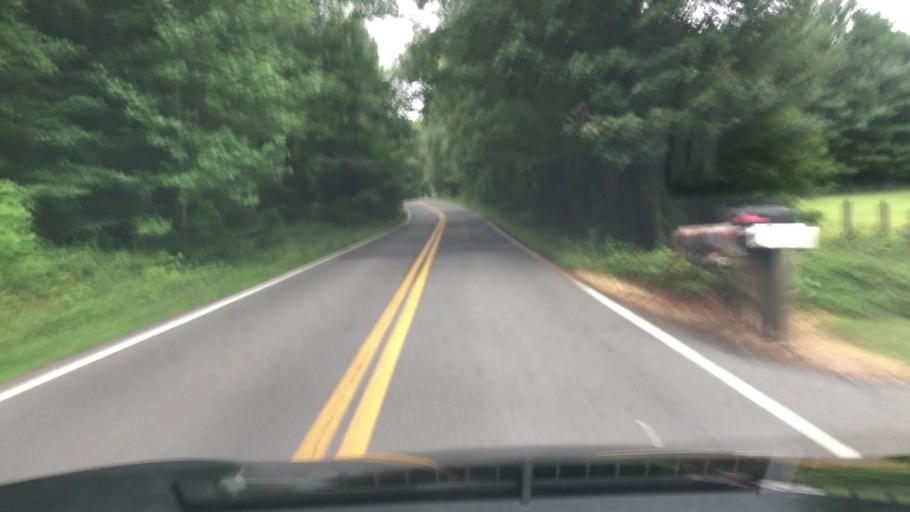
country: US
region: Virginia
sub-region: Fauquier County
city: Bealeton
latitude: 38.5335
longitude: -77.6115
